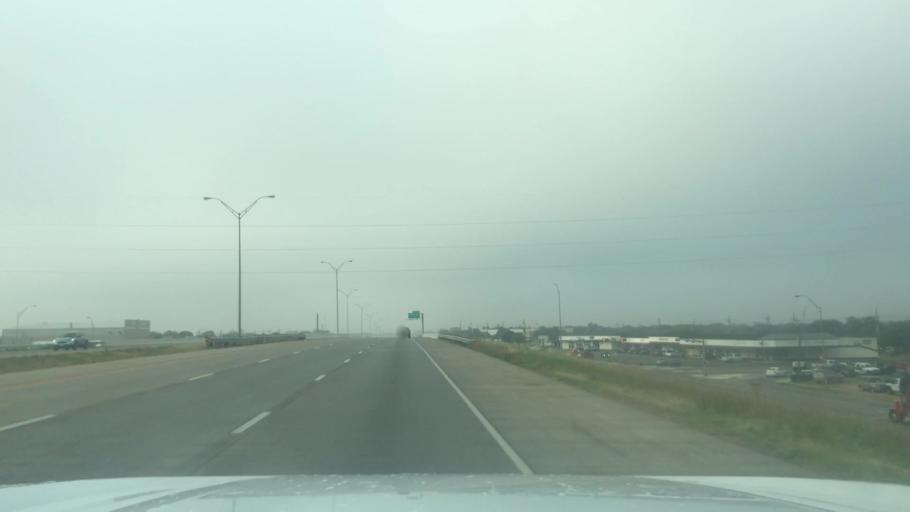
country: US
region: Texas
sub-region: Lubbock County
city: Lubbock
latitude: 33.5648
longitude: -101.8452
